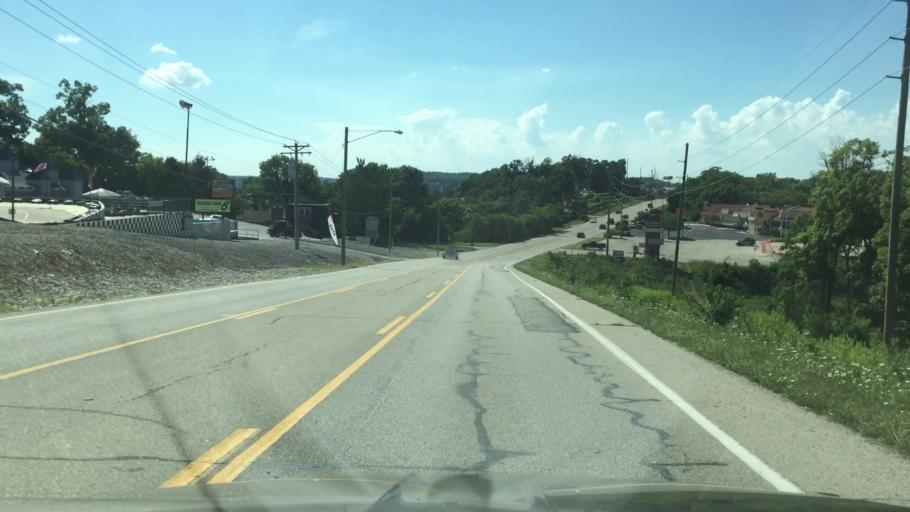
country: US
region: Missouri
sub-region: Miller County
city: Lake Ozark
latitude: 38.1825
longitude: -92.6328
